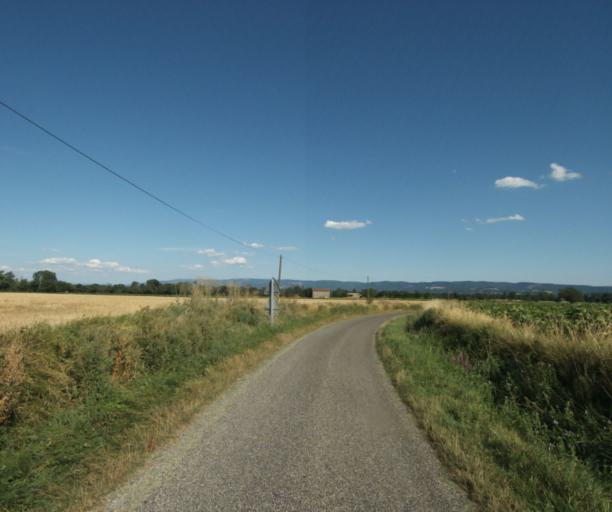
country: FR
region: Midi-Pyrenees
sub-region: Departement de la Haute-Garonne
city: Revel
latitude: 43.4894
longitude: 1.9457
